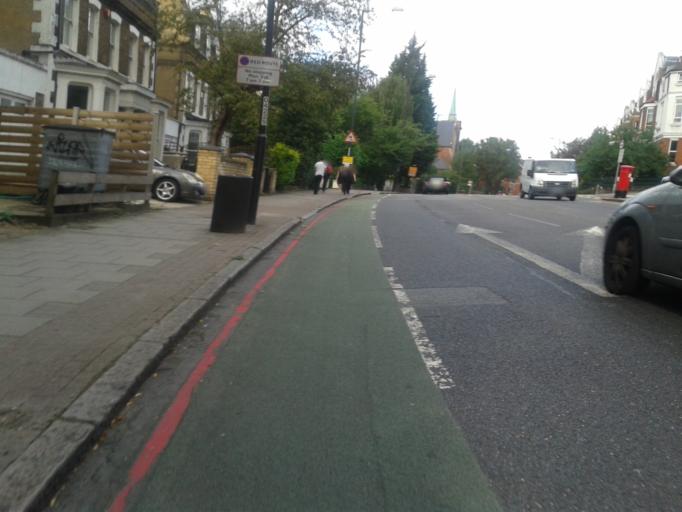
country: GB
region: England
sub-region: Greater London
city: Brixton Hill
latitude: 51.4393
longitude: -0.0994
